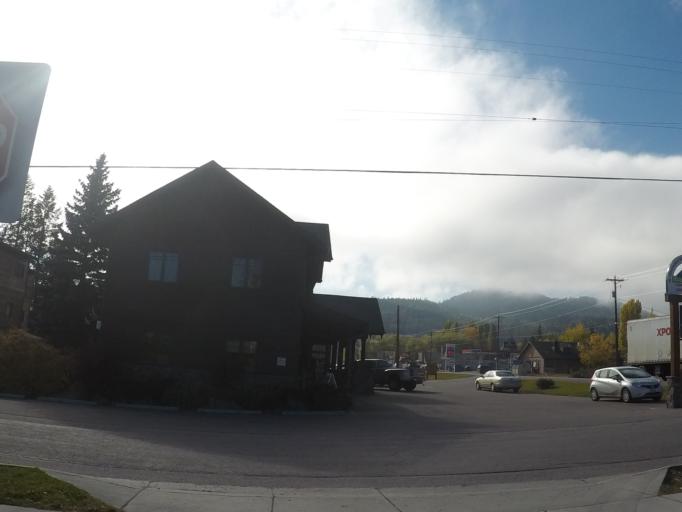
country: US
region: Montana
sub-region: Flathead County
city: Lakeside
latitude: 48.0196
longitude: -114.2243
